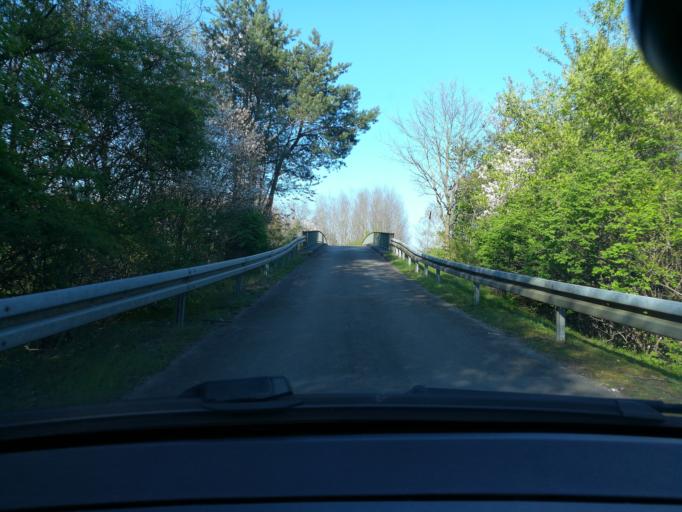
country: DE
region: North Rhine-Westphalia
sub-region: Regierungsbezirk Detmold
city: Verl
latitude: 51.9308
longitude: 8.5753
